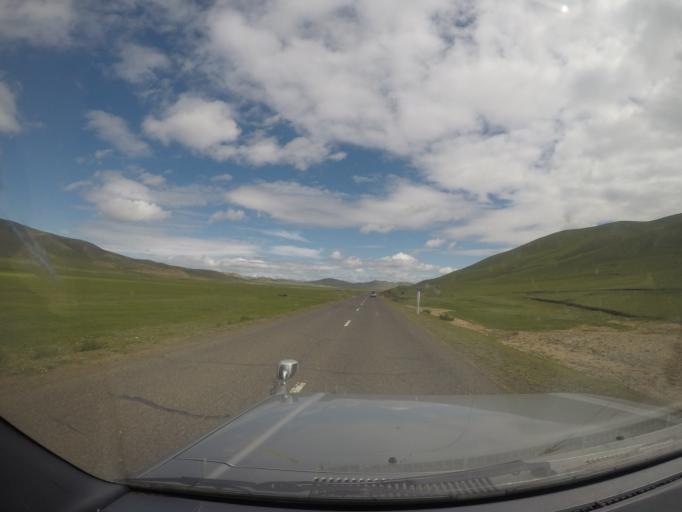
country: MN
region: Hentiy
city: Modot
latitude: 47.7038
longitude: 109.0688
